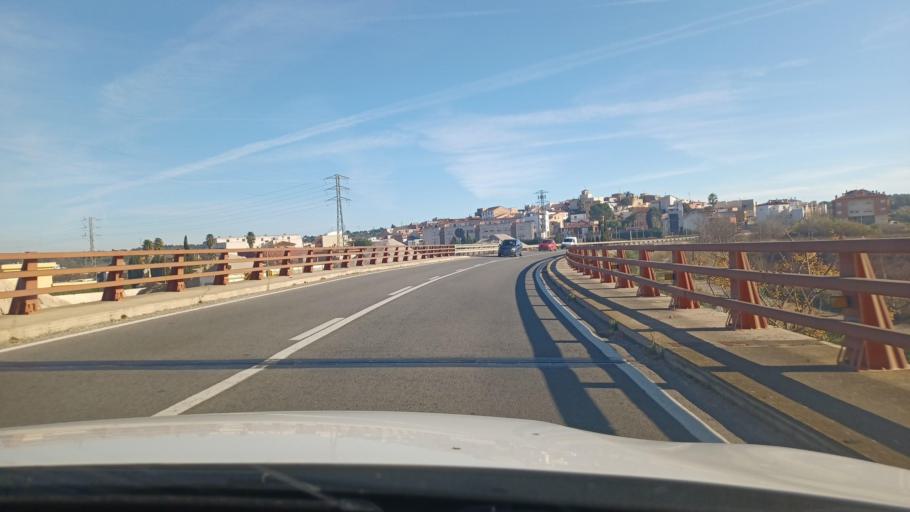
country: ES
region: Catalonia
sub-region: Provincia de Tarragona
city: Masdenverge
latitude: 40.7167
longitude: 0.5261
